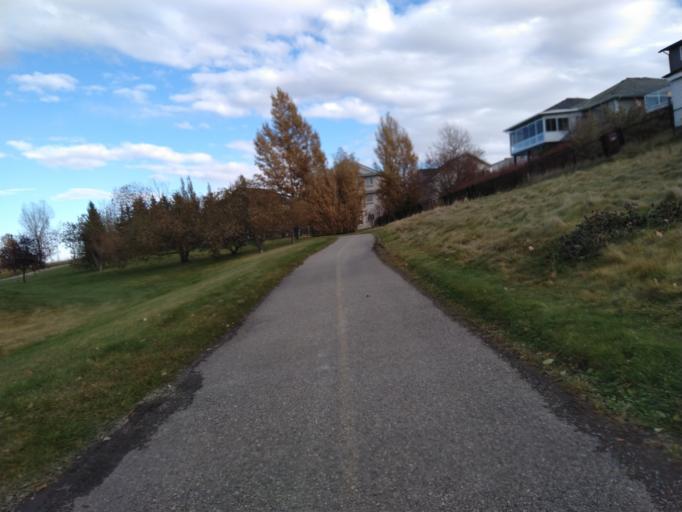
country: CA
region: Alberta
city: Calgary
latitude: 51.1393
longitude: -114.1243
